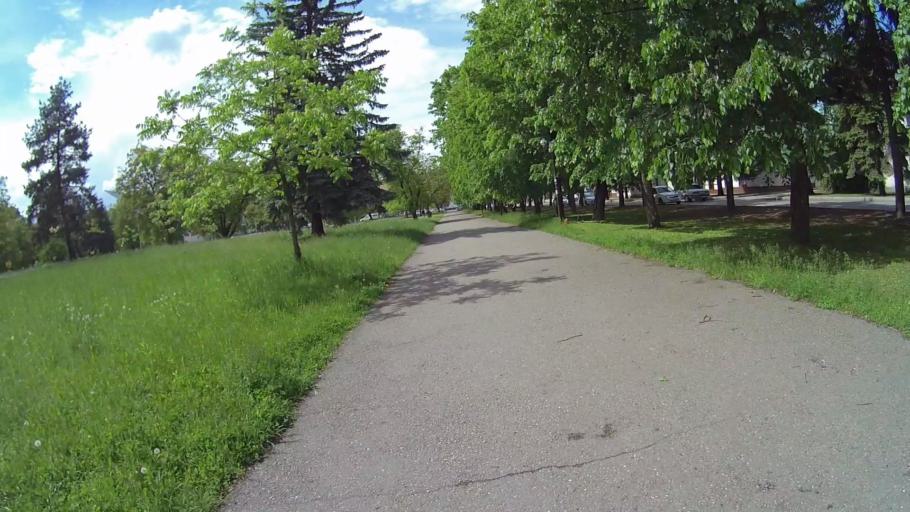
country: RU
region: Kabardino-Balkariya
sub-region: Gorod Nal'chik
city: Nal'chik
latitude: 43.4779
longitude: 43.5883
